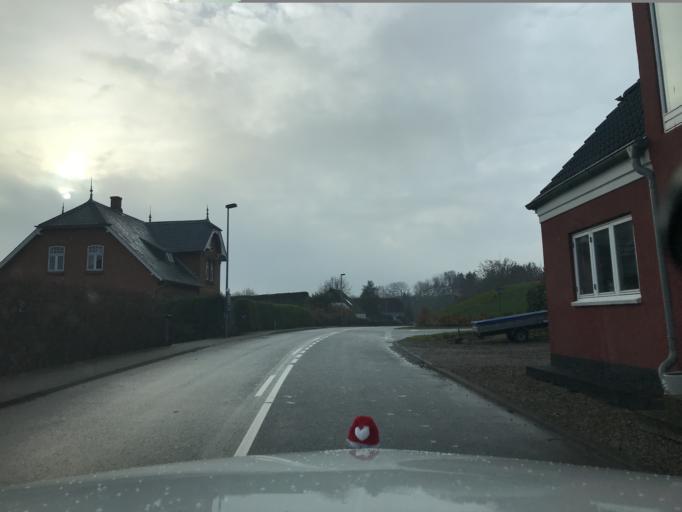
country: DK
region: South Denmark
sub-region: Sonderborg Kommune
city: Grasten
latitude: 54.8971
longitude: 9.5656
